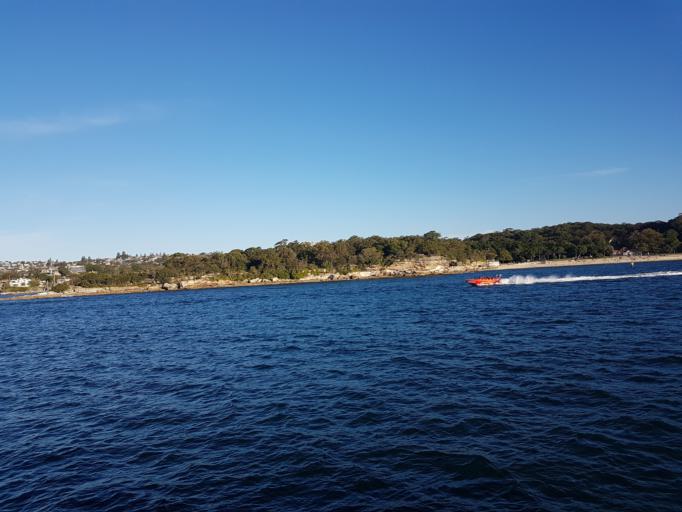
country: AU
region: New South Wales
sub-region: Woollahra
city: Point Piper
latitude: -33.8460
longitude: 151.2668
